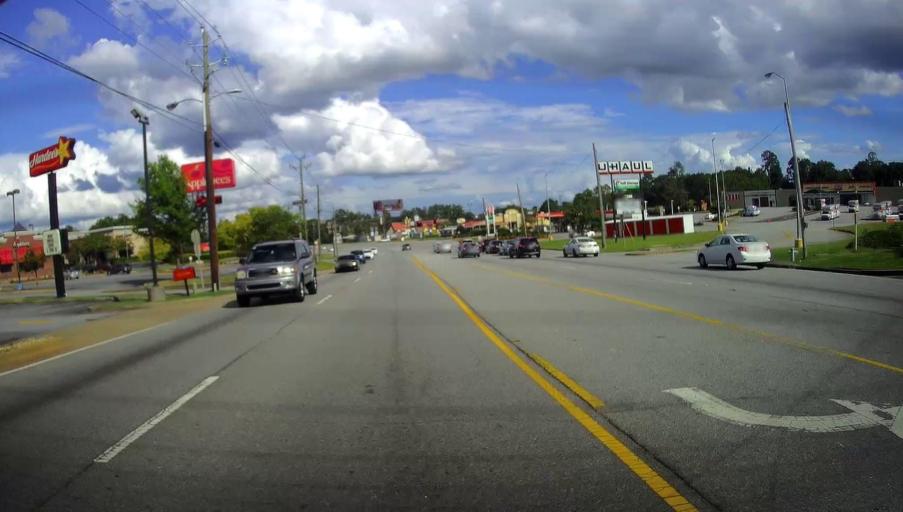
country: US
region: Alabama
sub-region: Russell County
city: Phenix City
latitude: 32.5202
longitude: -84.9581
